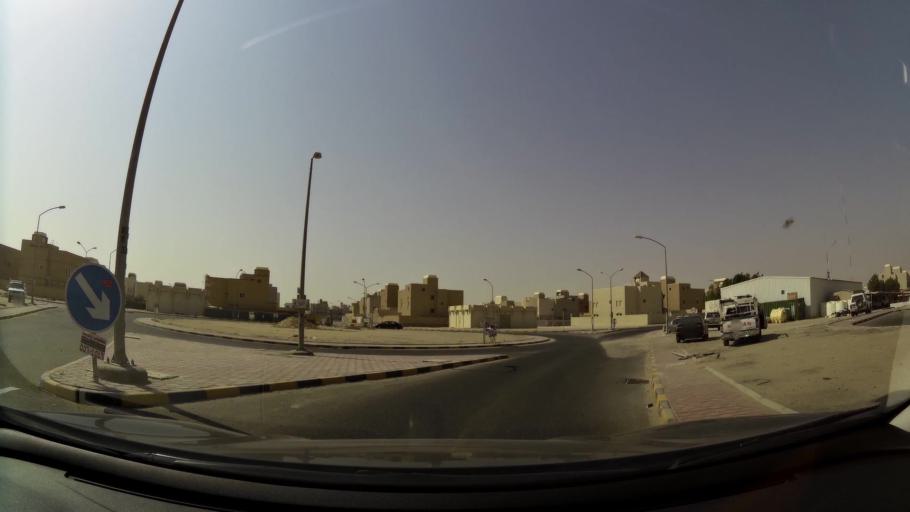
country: KW
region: Al Ahmadi
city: Al Wafrah
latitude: 28.8034
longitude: 48.0533
